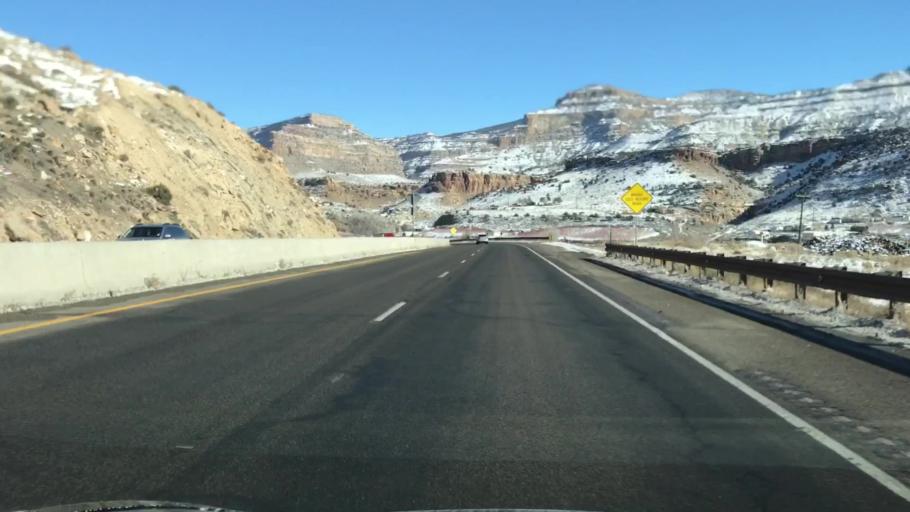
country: US
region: Colorado
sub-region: Mesa County
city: Palisade
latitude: 39.1185
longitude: -108.3269
